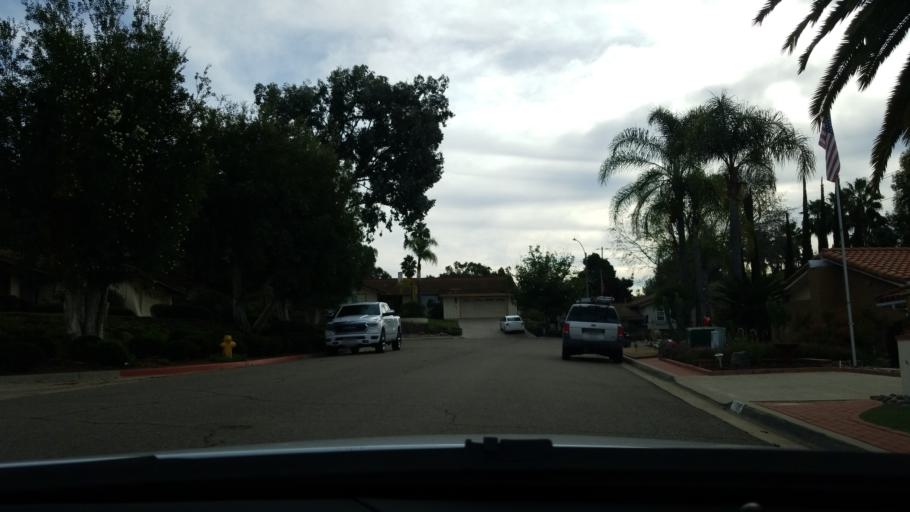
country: US
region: California
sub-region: San Diego County
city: Casa de Oro-Mount Helix
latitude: 32.7717
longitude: -116.9575
